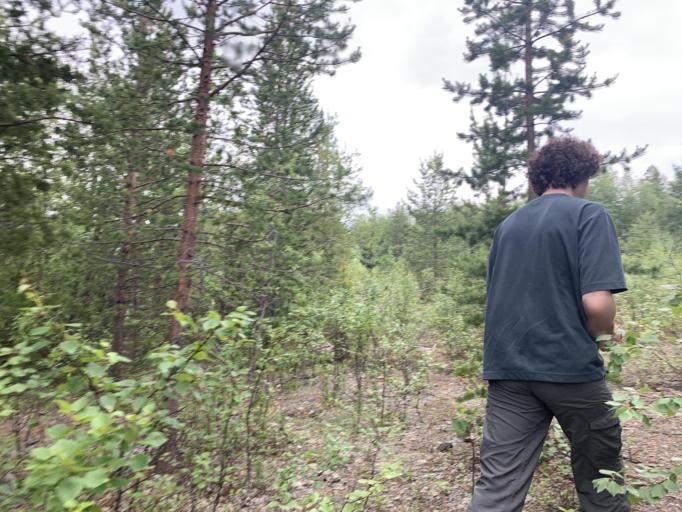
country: RU
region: Murmansk
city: Monchegorsk
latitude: 67.8764
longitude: 33.0815
